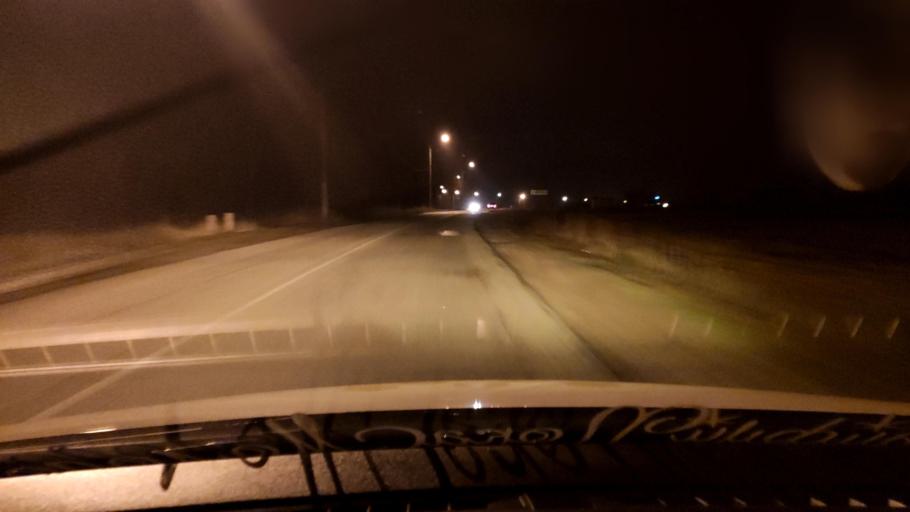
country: RU
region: Voronezj
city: Semiluki
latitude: 51.6566
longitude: 39.0400
